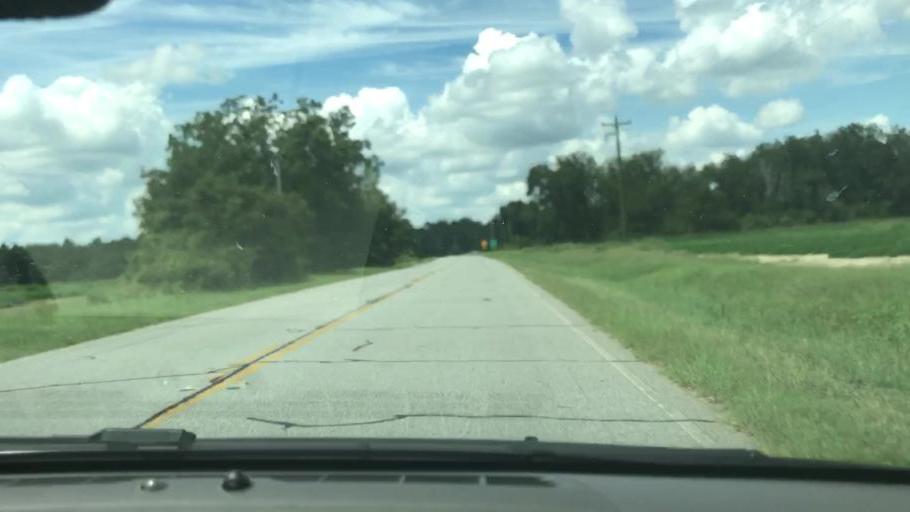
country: US
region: Georgia
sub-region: Stewart County
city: Lumpkin
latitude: 32.1419
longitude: -85.0092
